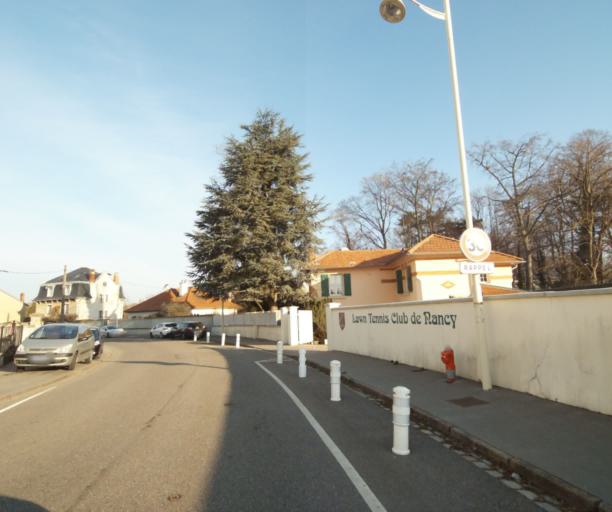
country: FR
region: Lorraine
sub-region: Departement de Meurthe-et-Moselle
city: Laxou
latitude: 48.6946
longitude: 6.1520
